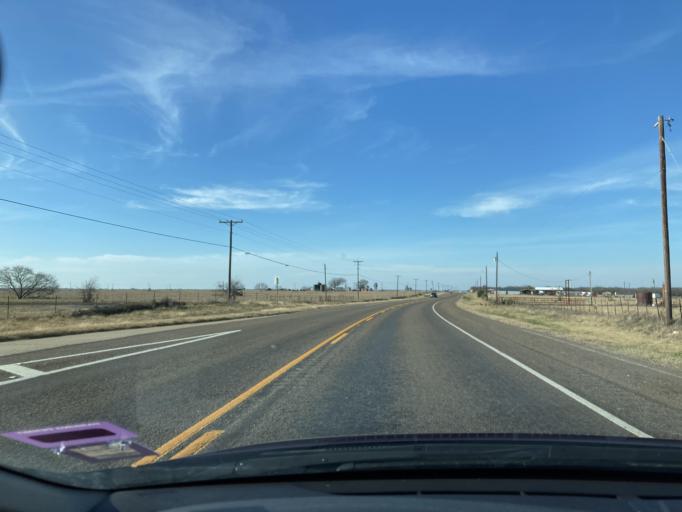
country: US
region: Texas
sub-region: Navarro County
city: Corsicana
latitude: 32.0379
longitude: -96.4056
